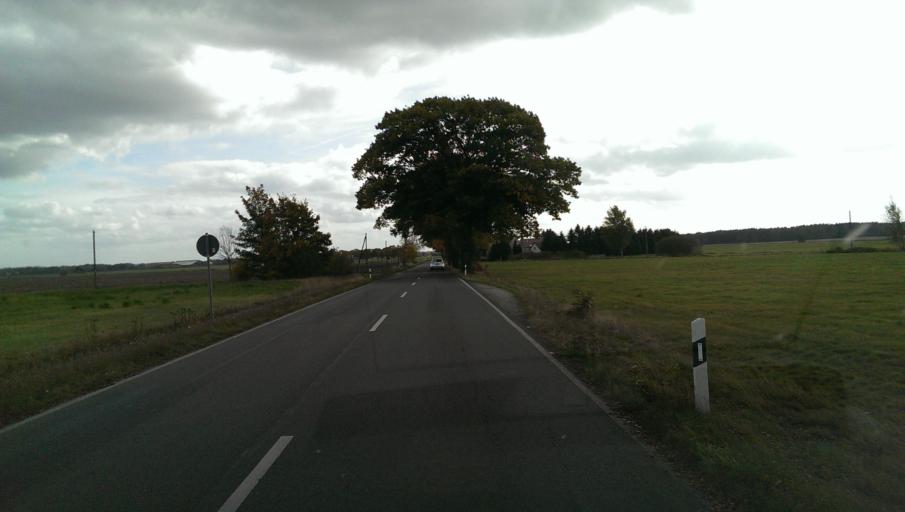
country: DE
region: Brandenburg
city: Grunewald
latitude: 51.4008
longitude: 14.0036
